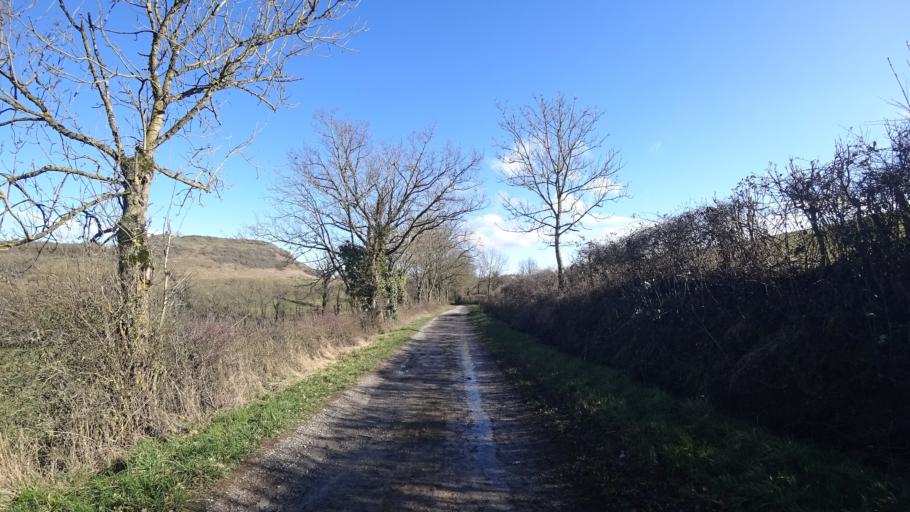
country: FR
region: Midi-Pyrenees
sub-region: Departement de l'Aveyron
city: Sainte-Radegonde
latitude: 44.3674
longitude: 2.6082
